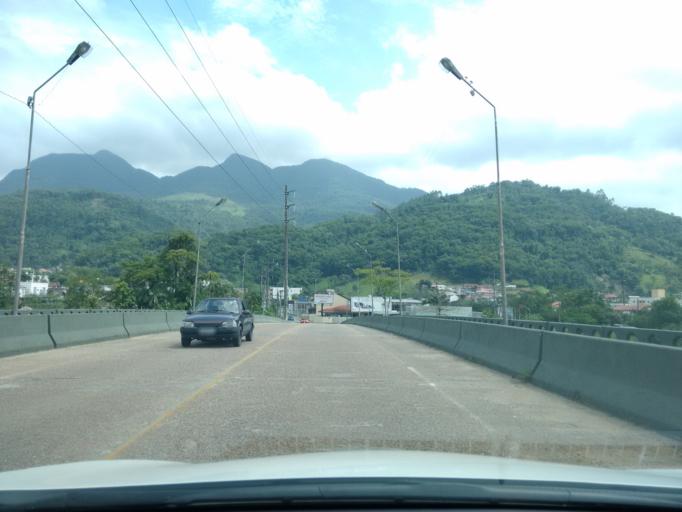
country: BR
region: Santa Catarina
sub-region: Jaragua Do Sul
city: Jaragua do Sul
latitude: -26.4871
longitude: -49.0566
